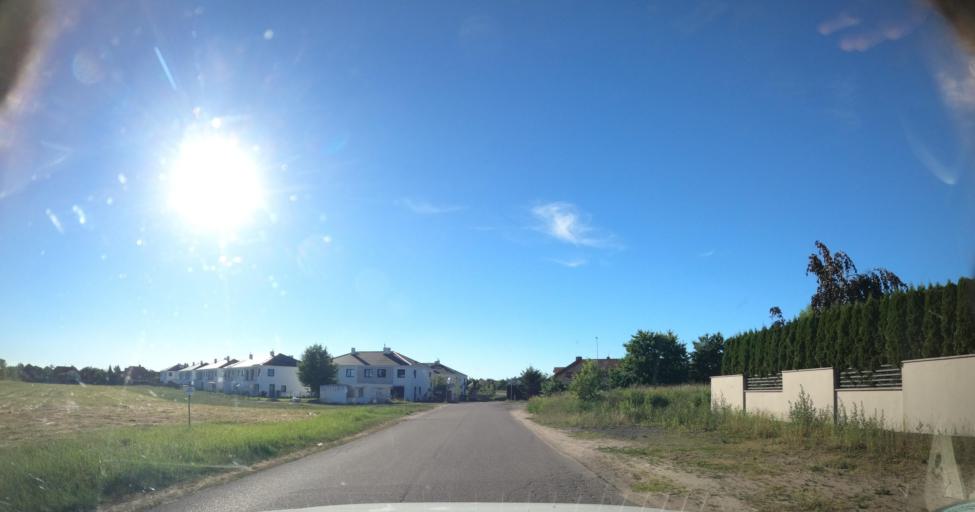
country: PL
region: West Pomeranian Voivodeship
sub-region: Szczecin
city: Szczecin
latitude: 53.4813
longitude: 14.5277
